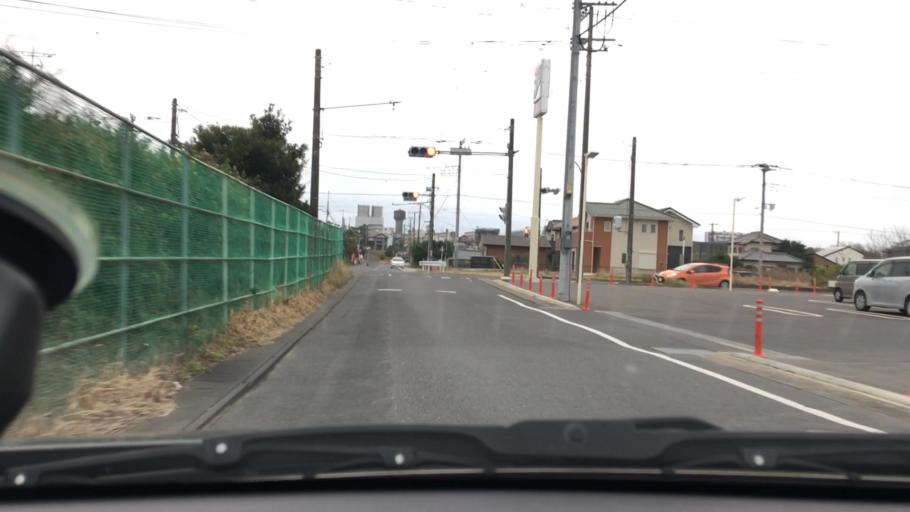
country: JP
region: Chiba
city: Omigawa
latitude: 35.8770
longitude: 140.7191
